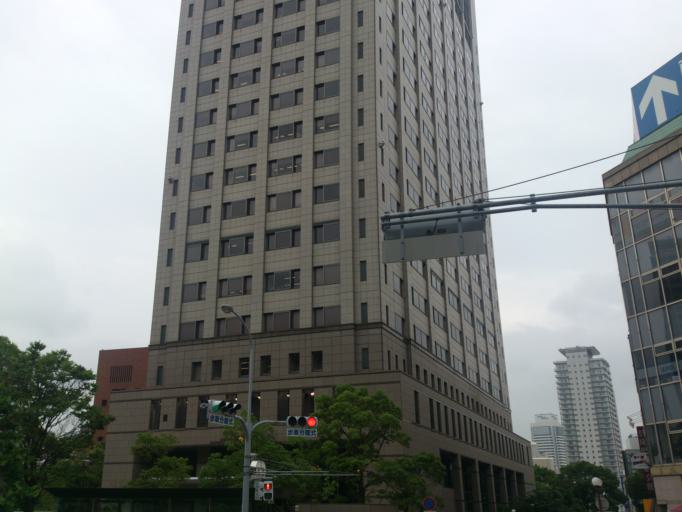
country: JP
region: Hyogo
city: Kobe
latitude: 34.6905
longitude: 135.1831
